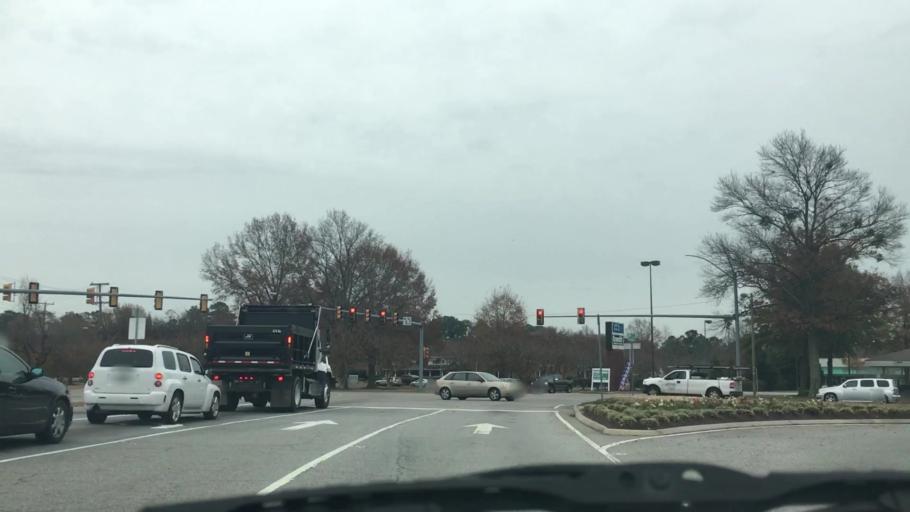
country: US
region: Virginia
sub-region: City of Portsmouth
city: Portsmouth Heights
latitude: 36.8609
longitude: -76.3920
